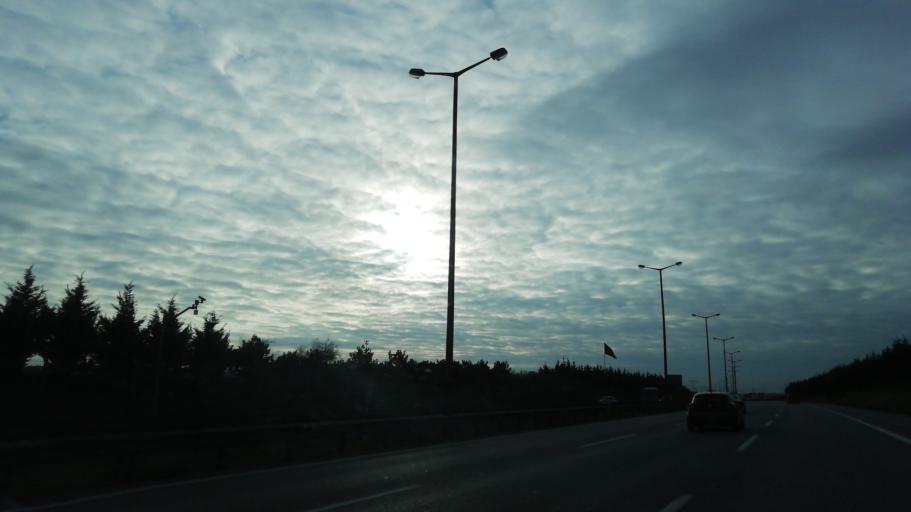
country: TR
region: Istanbul
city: Icmeler
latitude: 40.9199
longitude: 29.3518
